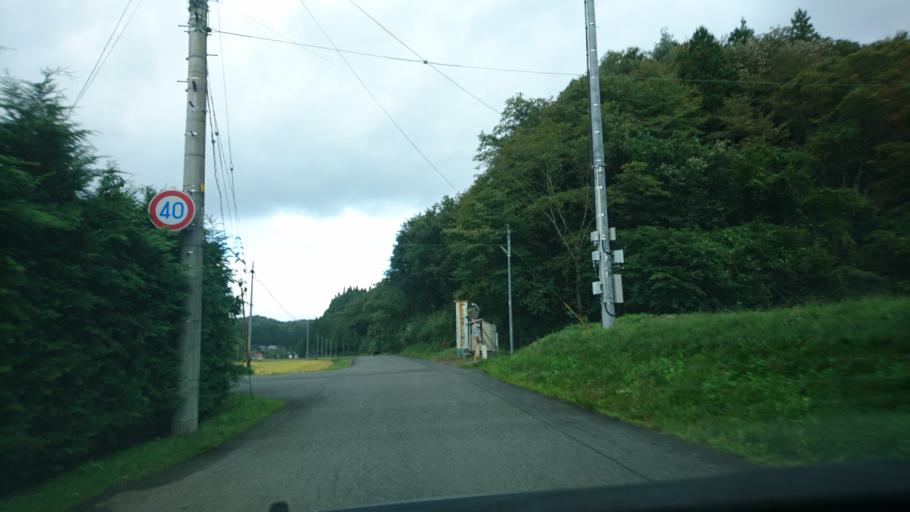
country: JP
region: Iwate
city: Ichinoseki
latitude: 38.8984
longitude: 141.0867
